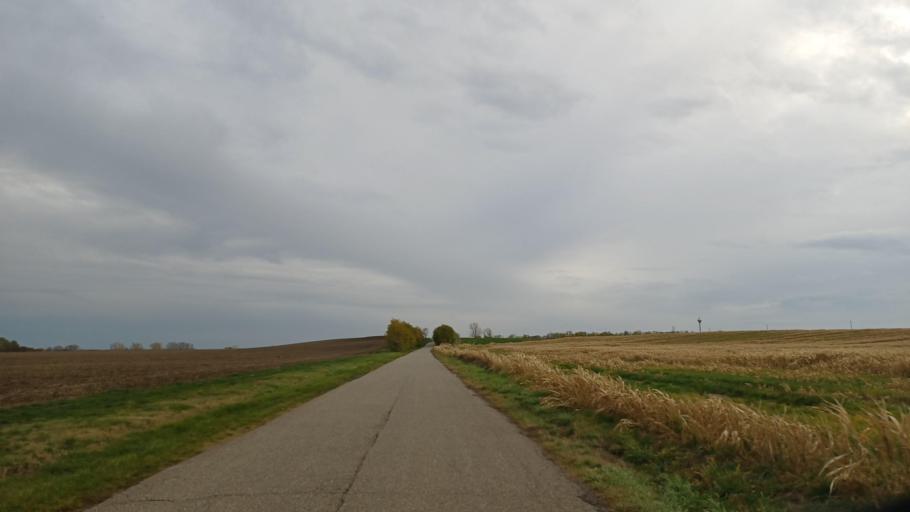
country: HU
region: Tolna
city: Nagydorog
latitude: 46.6443
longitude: 18.6070
